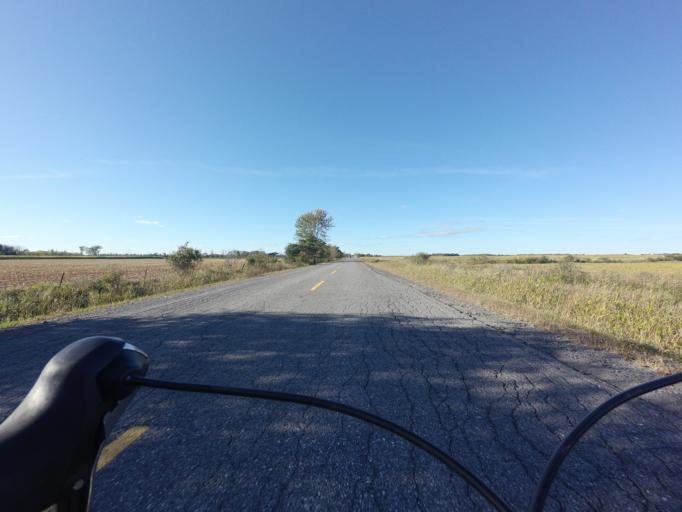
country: CA
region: Ontario
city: Bells Corners
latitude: 45.2006
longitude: -75.7906
